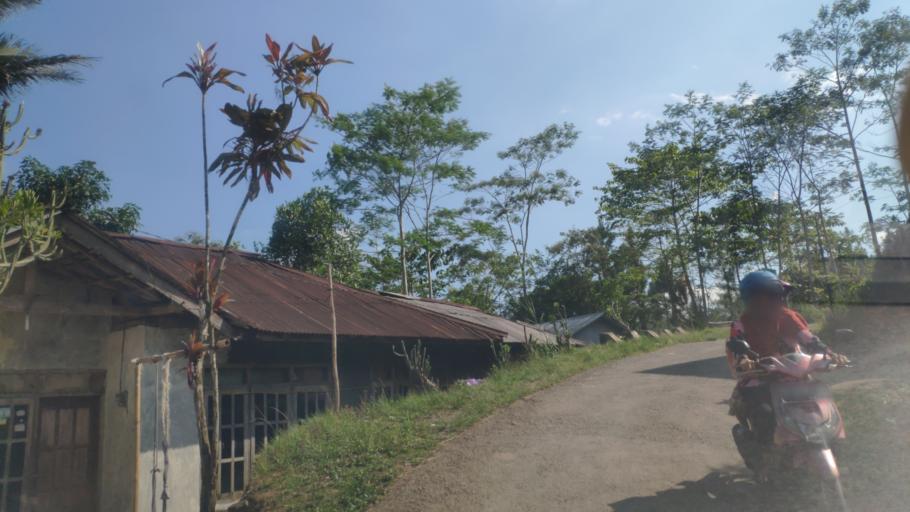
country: ID
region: Central Java
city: Buaran
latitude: -7.2258
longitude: 109.5904
